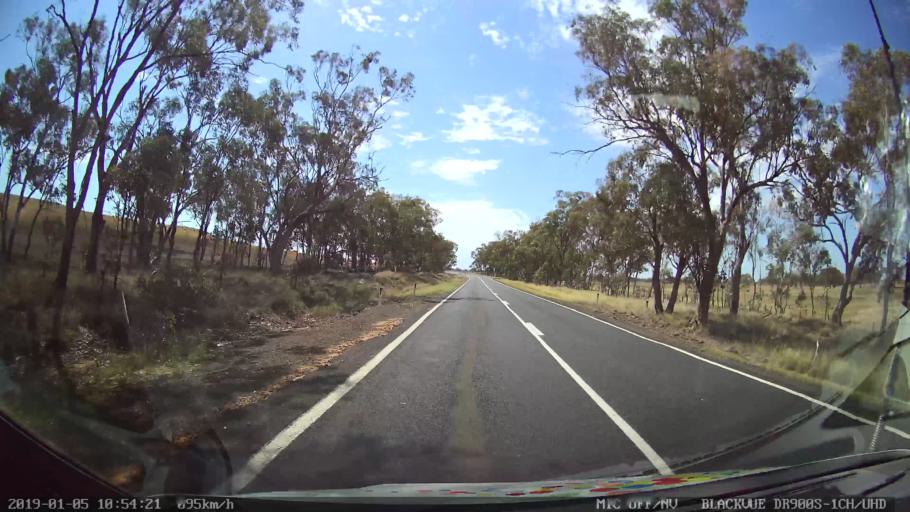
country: AU
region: New South Wales
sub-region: Warrumbungle Shire
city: Coonabarabran
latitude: -31.4495
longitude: 149.1269
